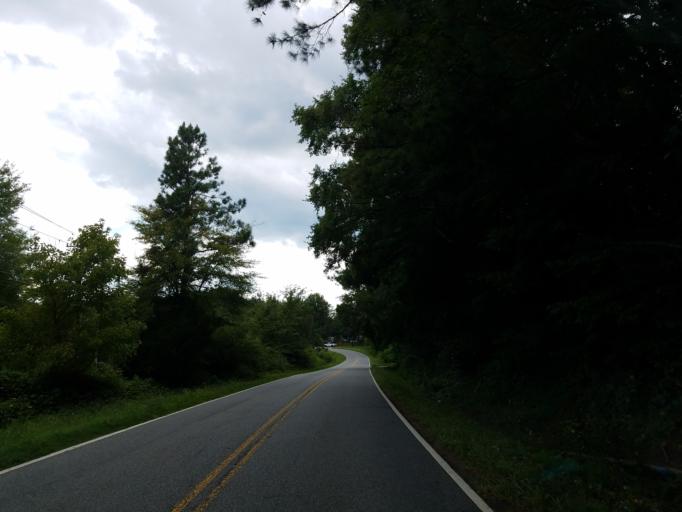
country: US
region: Georgia
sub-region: Bartow County
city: Cartersville
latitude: 34.2575
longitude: -84.8428
